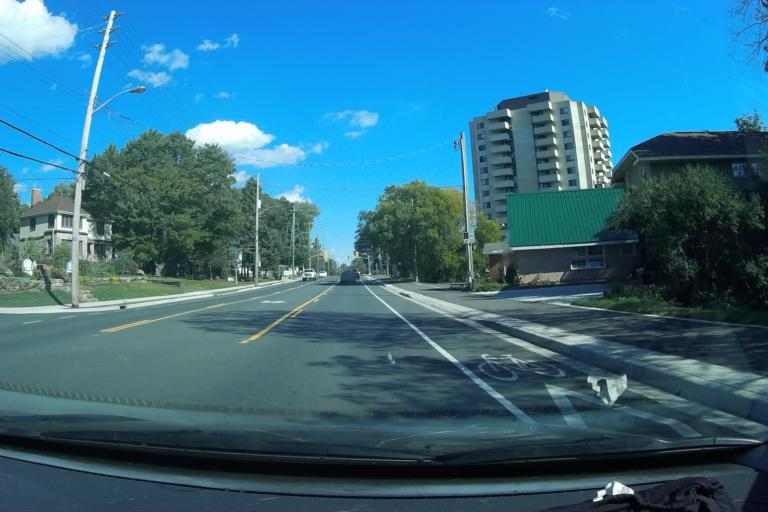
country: CA
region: Ontario
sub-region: Algoma
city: Sault Ste. Marie
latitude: 46.5049
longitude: -84.3095
